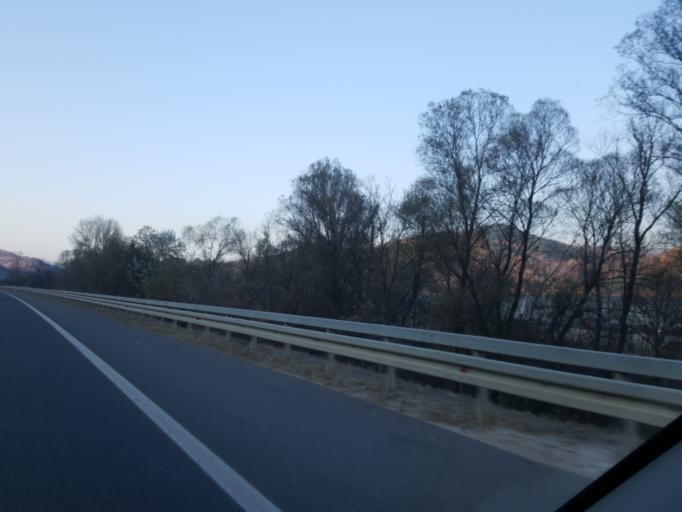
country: RS
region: Central Serbia
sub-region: Pirotski Okrug
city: Pirot
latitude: 43.1740
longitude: 22.5721
